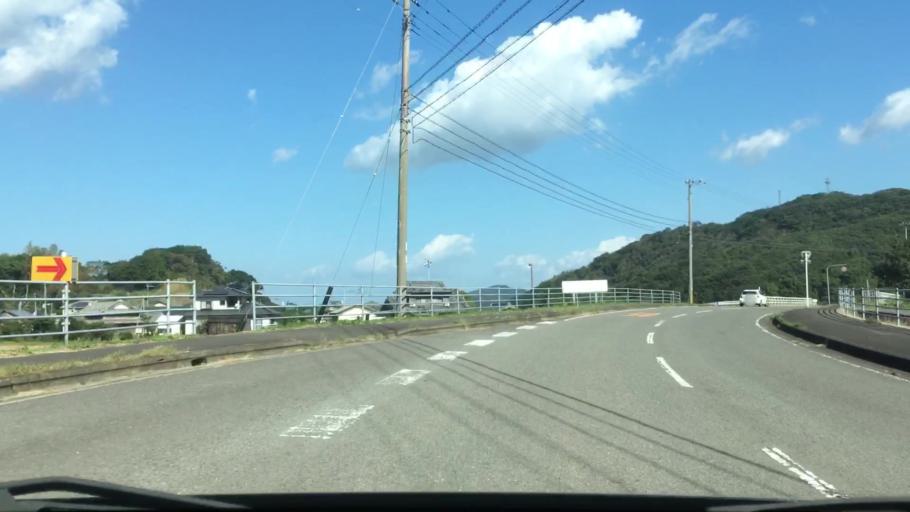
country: JP
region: Nagasaki
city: Sasebo
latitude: 32.9875
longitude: 129.6456
